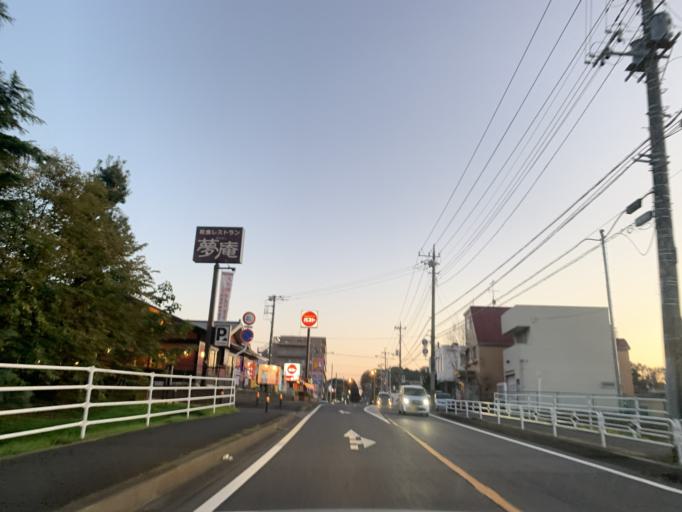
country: JP
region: Chiba
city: Nagareyama
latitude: 35.8926
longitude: 139.9007
